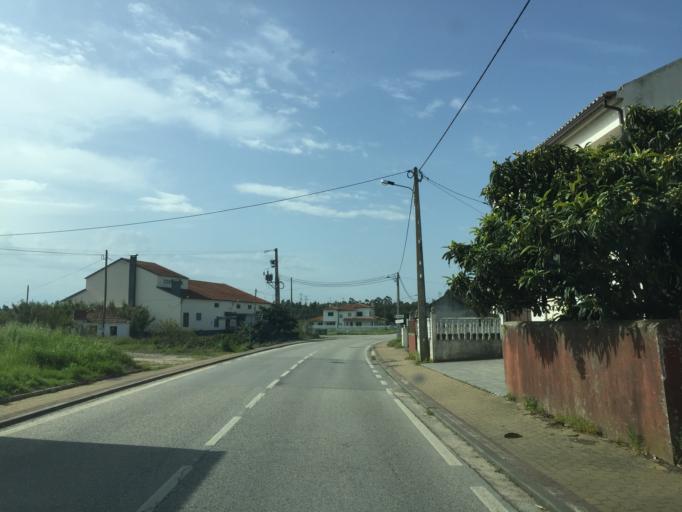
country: PT
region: Coimbra
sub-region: Figueira da Foz
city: Lavos
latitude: 40.0563
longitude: -8.8144
